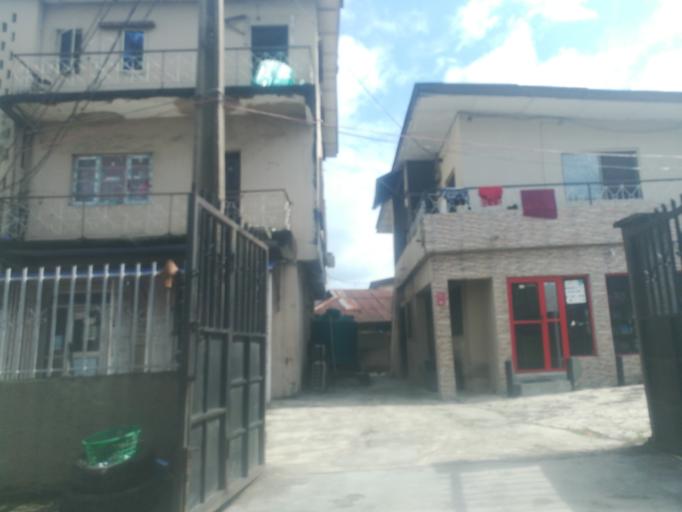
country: NG
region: Lagos
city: Somolu
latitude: 6.5493
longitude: 3.3694
